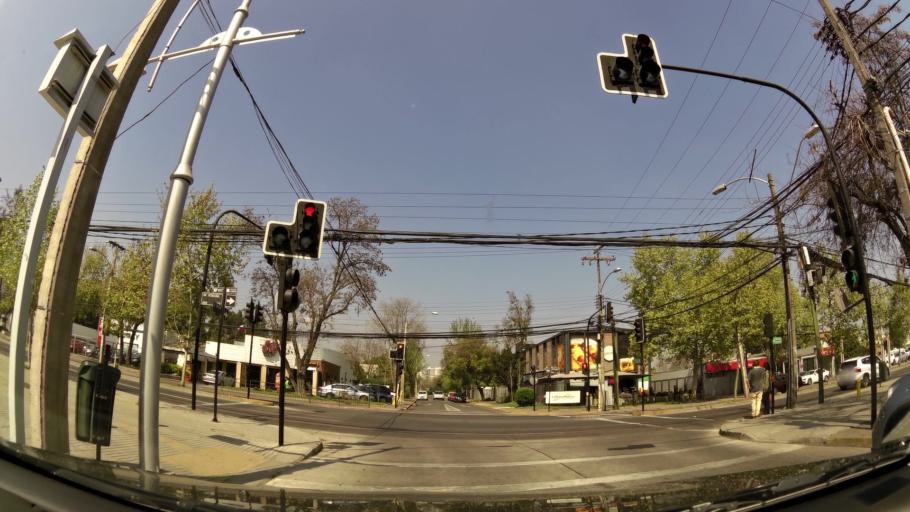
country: CL
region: Santiago Metropolitan
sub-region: Provincia de Santiago
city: Villa Presidente Frei, Nunoa, Santiago, Chile
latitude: -33.3879
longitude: -70.5667
